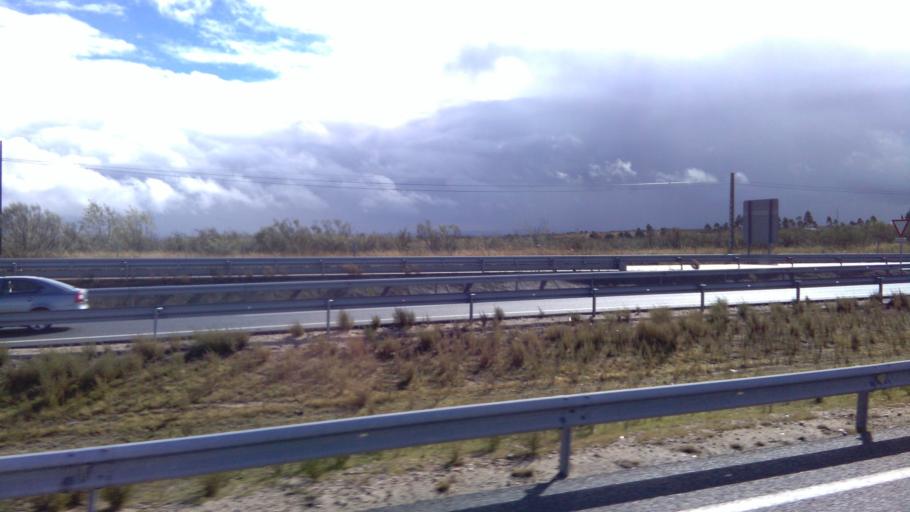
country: ES
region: Castille-La Mancha
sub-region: Province of Toledo
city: Valmojado
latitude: 40.2444
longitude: -4.0591
